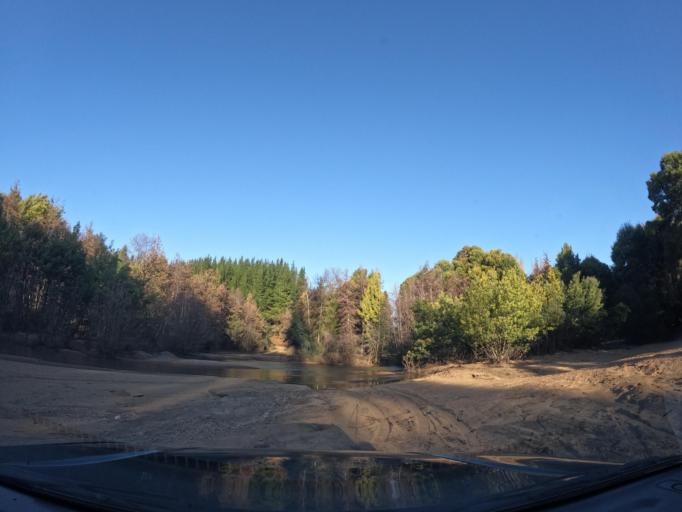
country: CL
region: Biobio
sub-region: Provincia de Concepcion
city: Chiguayante
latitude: -37.0385
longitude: -72.8293
